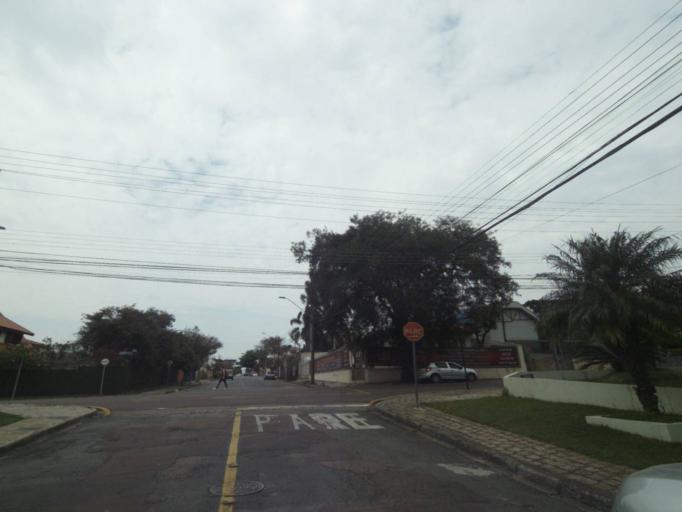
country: BR
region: Parana
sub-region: Curitiba
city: Curitiba
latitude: -25.4560
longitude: -49.3077
